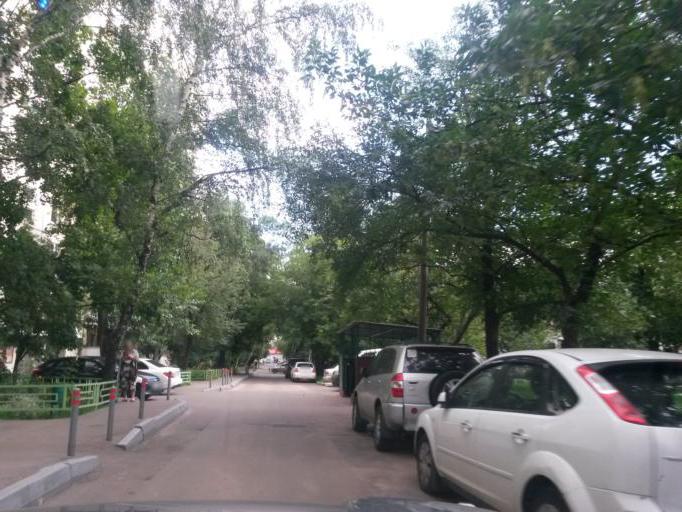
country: RU
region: Moscow
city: Orekhovo-Borisovo
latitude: 55.6082
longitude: 37.7164
